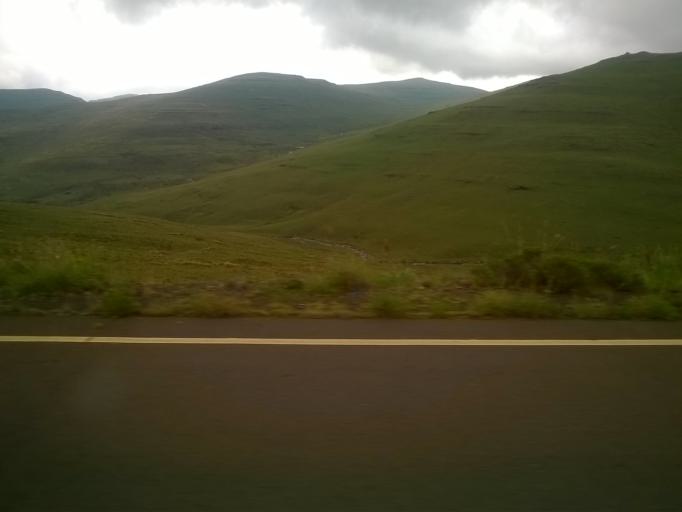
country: LS
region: Butha-Buthe
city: Butha-Buthe
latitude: -29.0941
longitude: 28.4247
